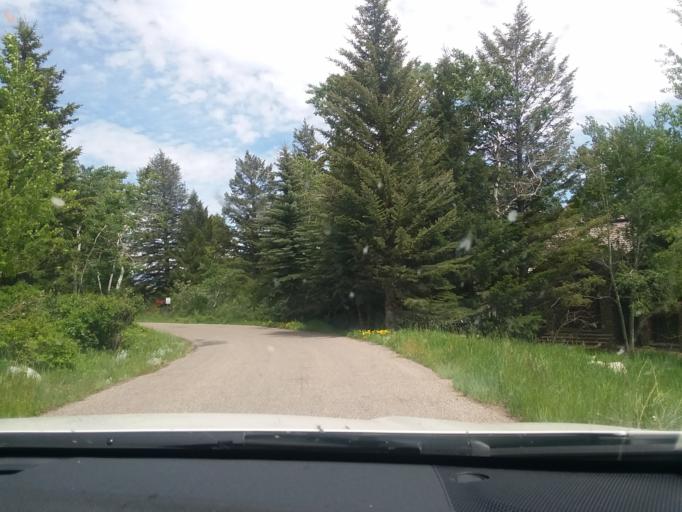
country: US
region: Wyoming
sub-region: Teton County
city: Moose Wilson Road
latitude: 43.5860
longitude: -110.8358
